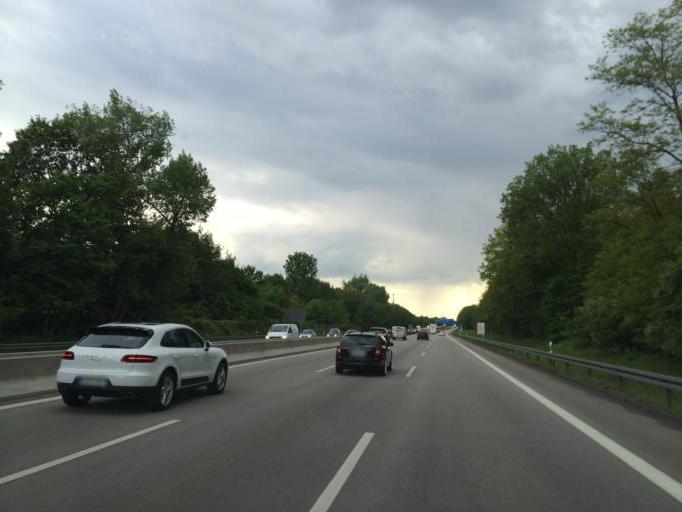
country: DE
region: Berlin
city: Grunewald
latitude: 52.4760
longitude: 13.2446
